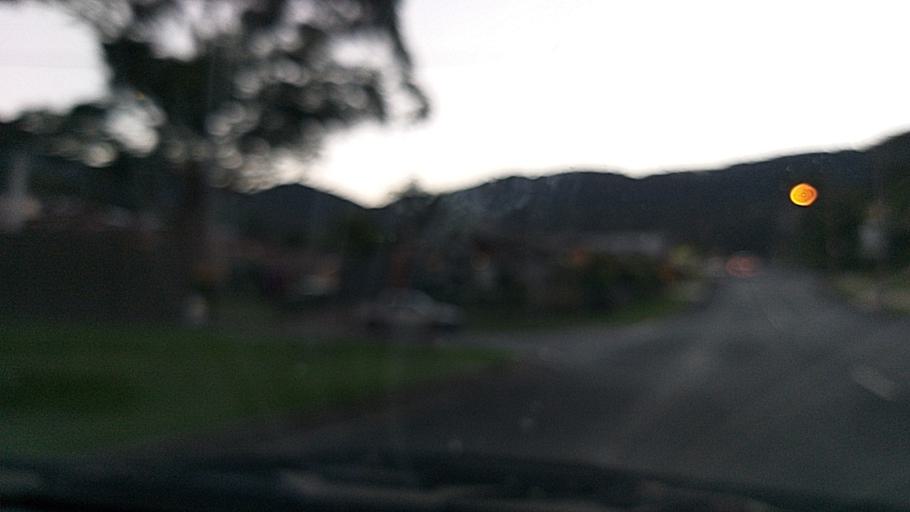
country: AU
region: New South Wales
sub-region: Wollongong
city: Mount Ousley
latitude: -34.3881
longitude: 150.8736
